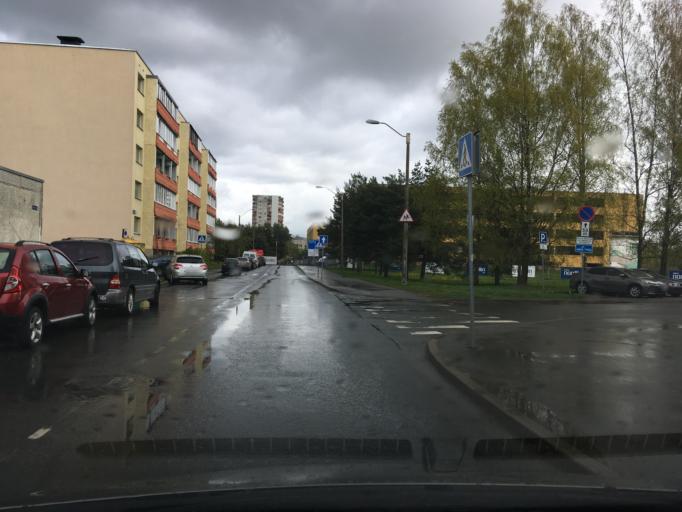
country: EE
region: Harju
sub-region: Tallinna linn
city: Kose
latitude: 59.4431
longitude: 24.8946
